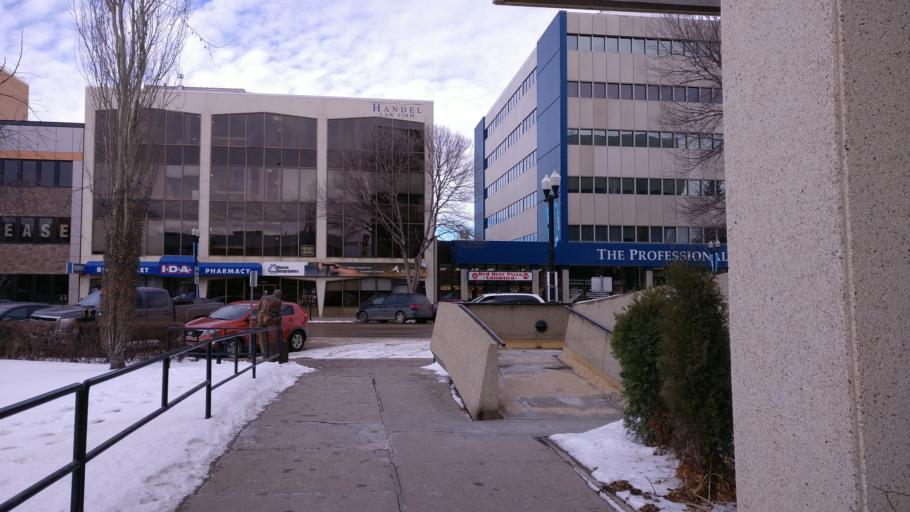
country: CA
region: Alberta
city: Red Deer
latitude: 52.2687
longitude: -113.8099
